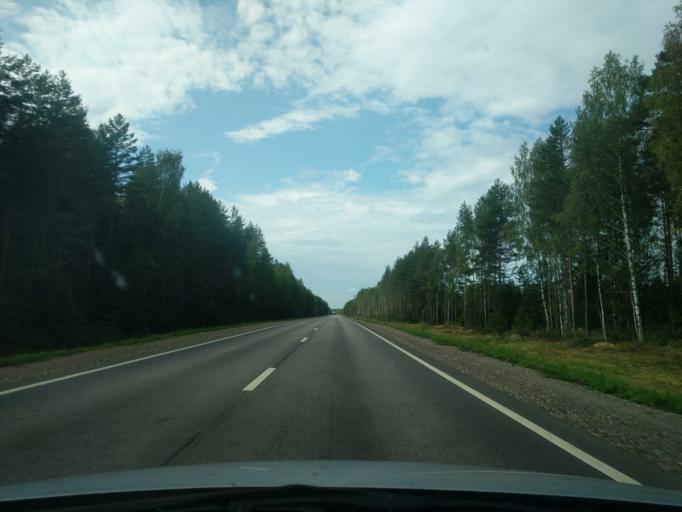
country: RU
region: Kostroma
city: Kadyy
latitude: 57.7969
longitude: 42.9045
